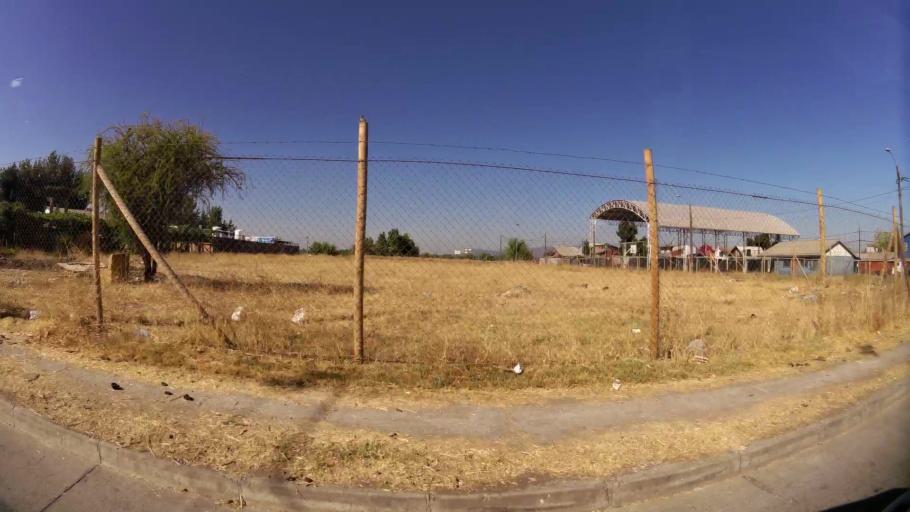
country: CL
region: Maule
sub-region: Provincia de Curico
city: Curico
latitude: -34.9965
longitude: -71.2588
